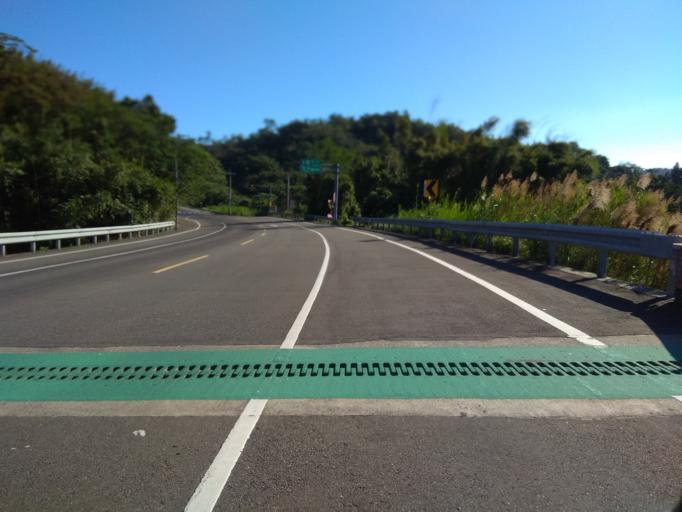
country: TW
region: Taiwan
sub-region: Hsinchu
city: Zhubei
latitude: 24.8480
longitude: 121.1152
